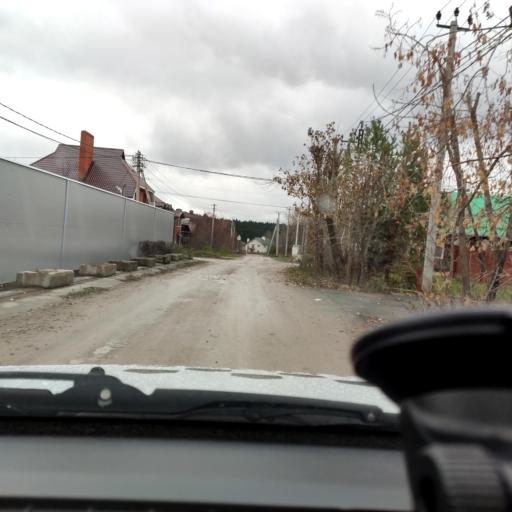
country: RU
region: Perm
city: Perm
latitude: 57.9893
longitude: 56.3065
